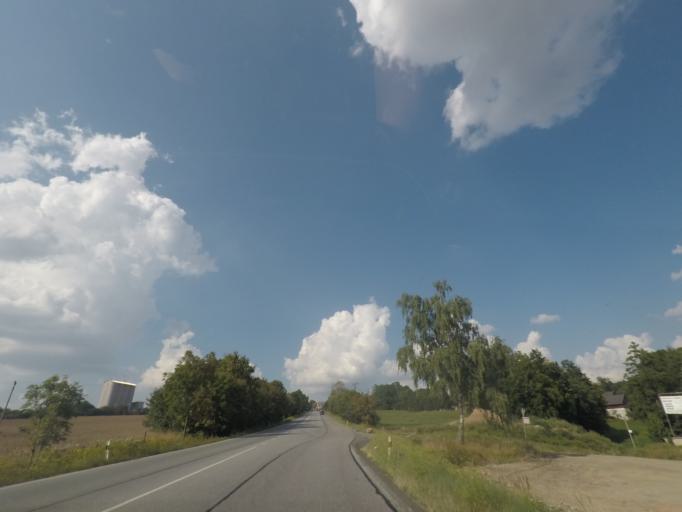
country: CZ
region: Kralovehradecky
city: Dvur Kralove nad Labem
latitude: 50.4475
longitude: 15.8569
